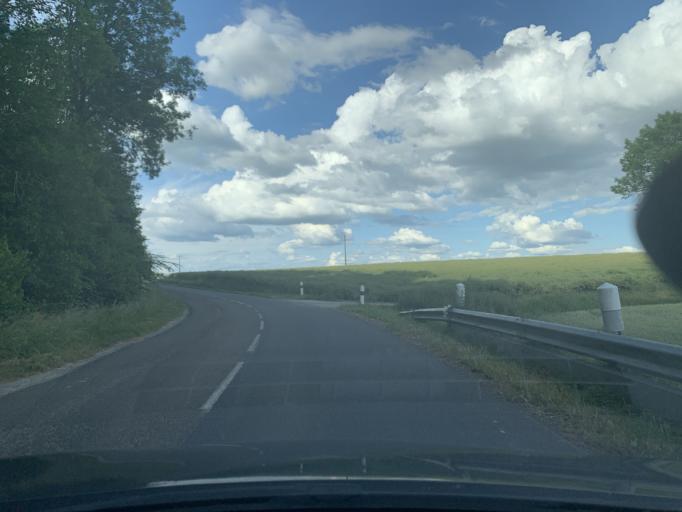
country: FR
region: Nord-Pas-de-Calais
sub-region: Departement du Nord
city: Gouzeaucourt
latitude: 50.0897
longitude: 3.1464
